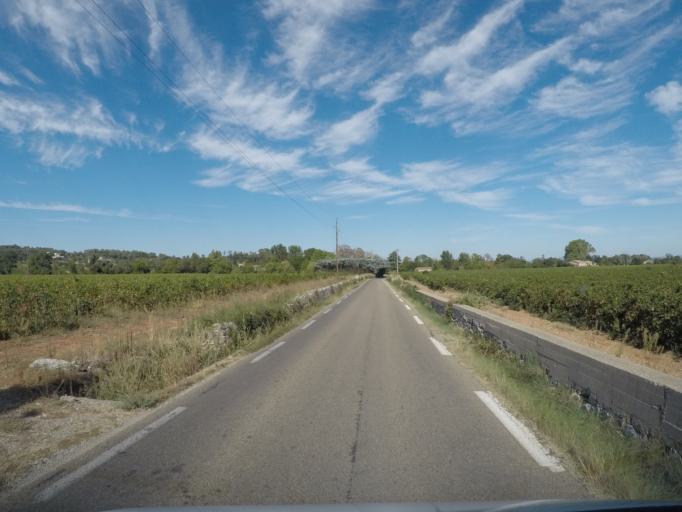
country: FR
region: Languedoc-Roussillon
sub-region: Departement du Gard
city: Boisset-et-Gaujac
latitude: 44.0162
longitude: 3.9921
